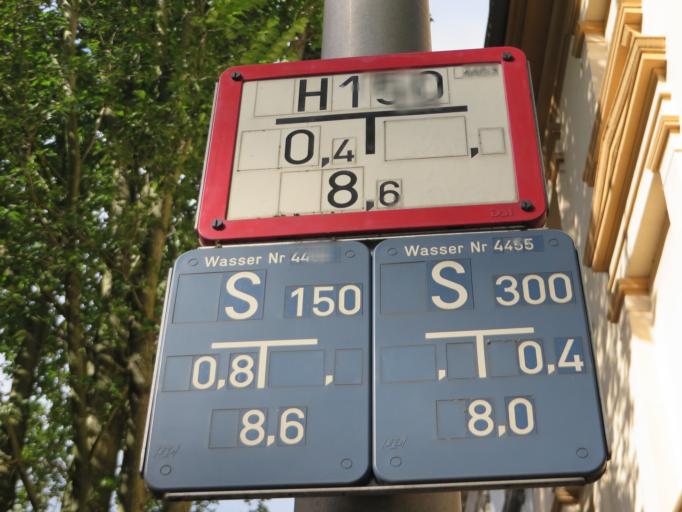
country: DE
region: North Rhine-Westphalia
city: Witten
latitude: 51.4411
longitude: 7.3252
